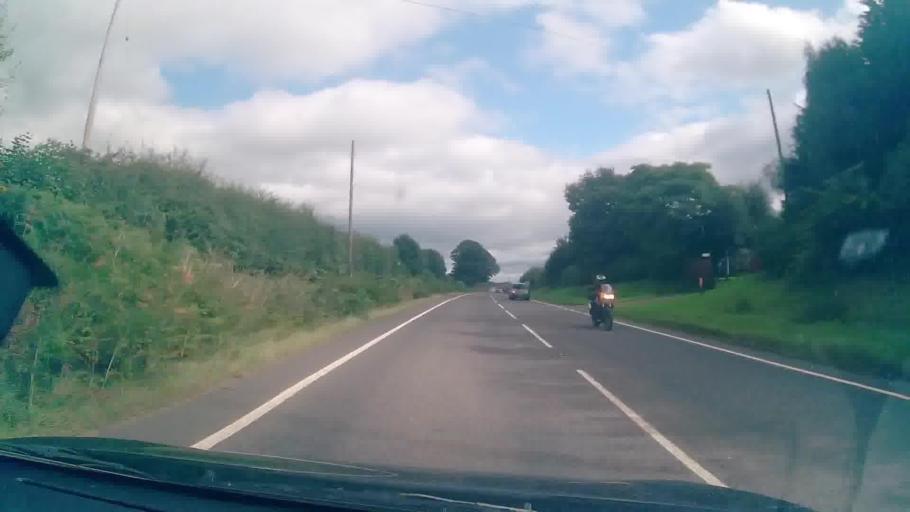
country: GB
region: England
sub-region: Shropshire
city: Whitchurch
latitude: 52.9658
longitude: -2.7237
